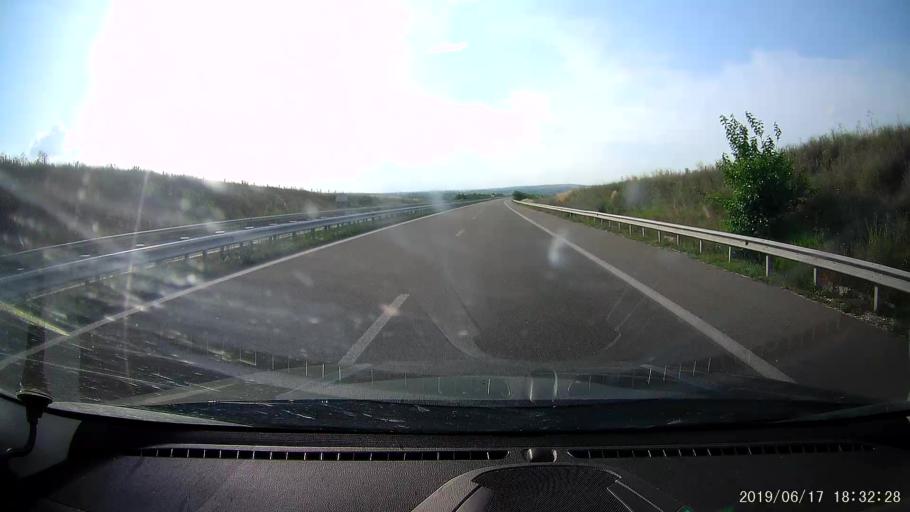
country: BG
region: Khaskovo
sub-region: Obshtina Dimitrovgrad
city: Dimitrovgrad
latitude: 42.0604
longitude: 25.4780
